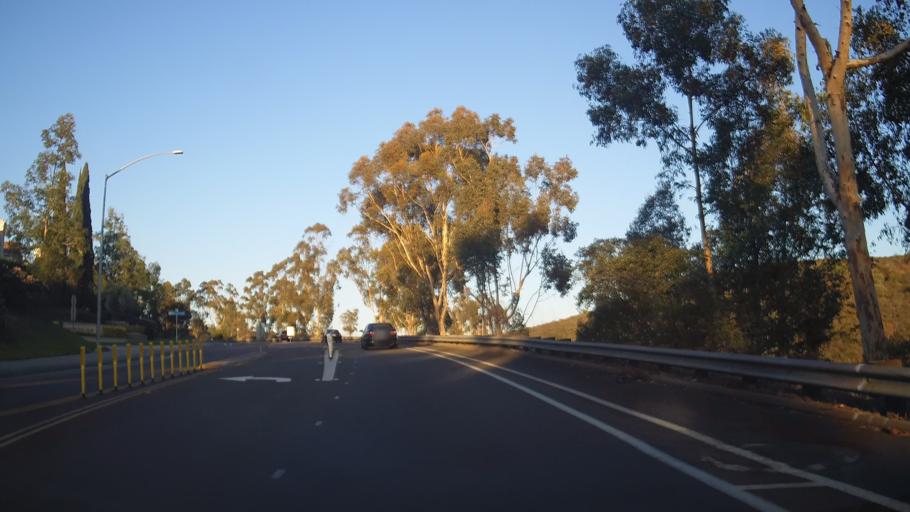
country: US
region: California
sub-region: San Diego County
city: Poway
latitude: 32.9189
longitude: -117.0656
